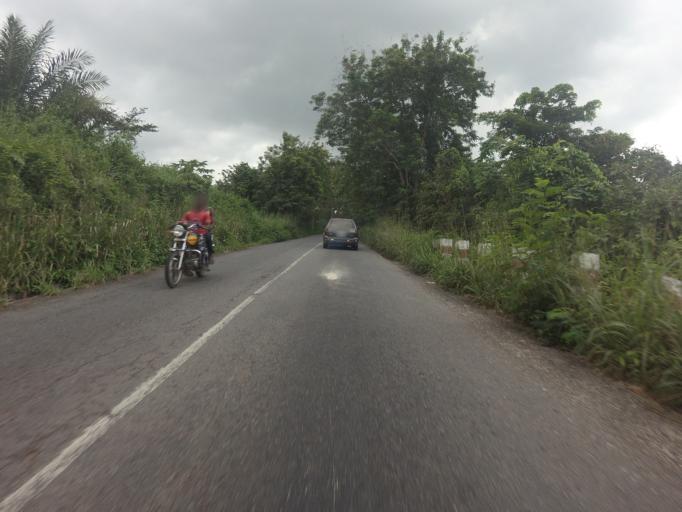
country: GH
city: Akropong
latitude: 5.9584
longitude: -0.1149
